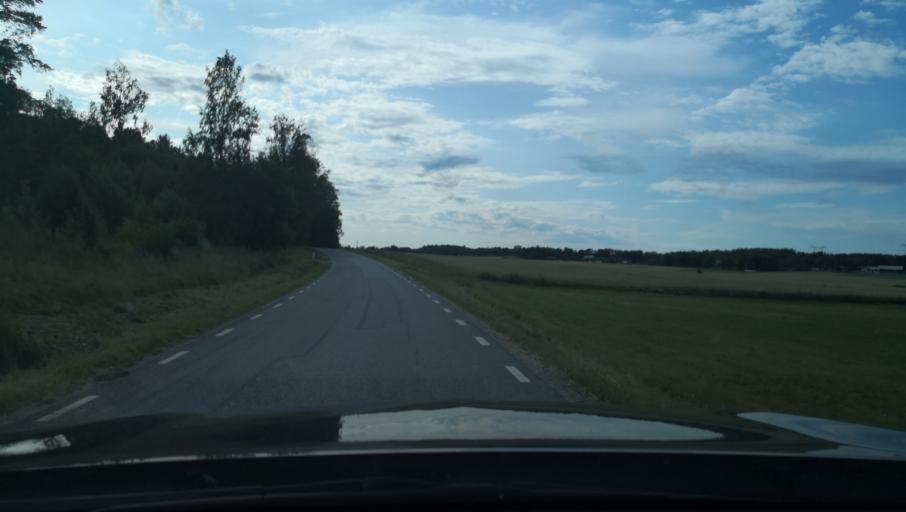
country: SE
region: Uppsala
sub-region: Enkopings Kommun
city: Orsundsbro
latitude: 59.6922
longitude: 17.3561
